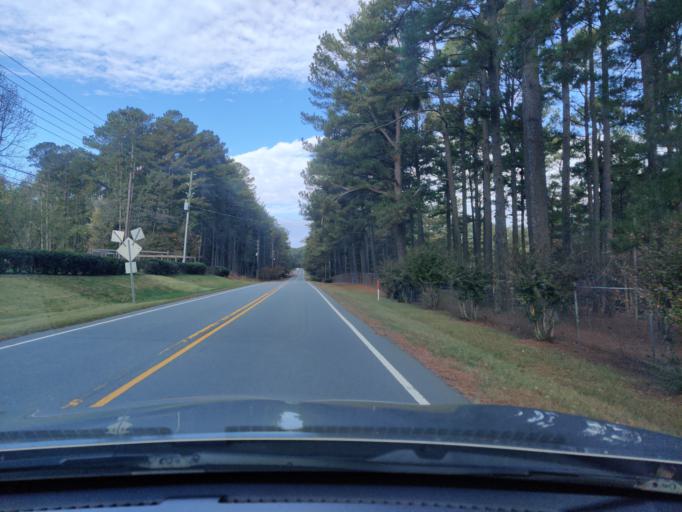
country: US
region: North Carolina
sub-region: Wake County
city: West Raleigh
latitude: 35.9180
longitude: -78.7133
